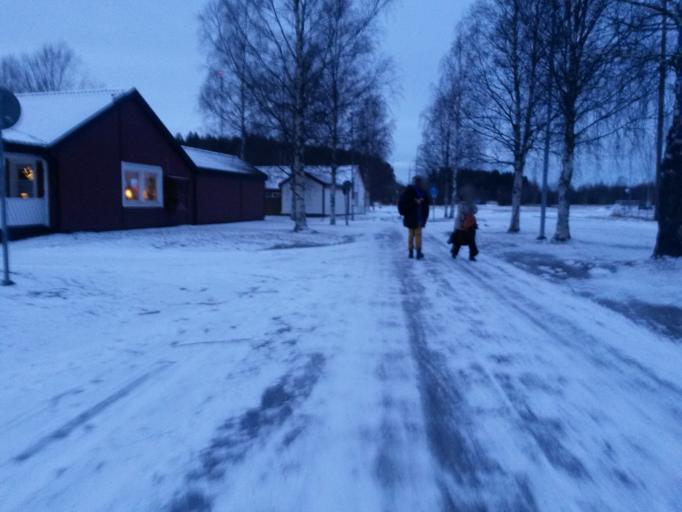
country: SE
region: Vaesterbotten
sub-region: Umea Kommun
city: Umea
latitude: 63.8414
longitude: 20.2172
